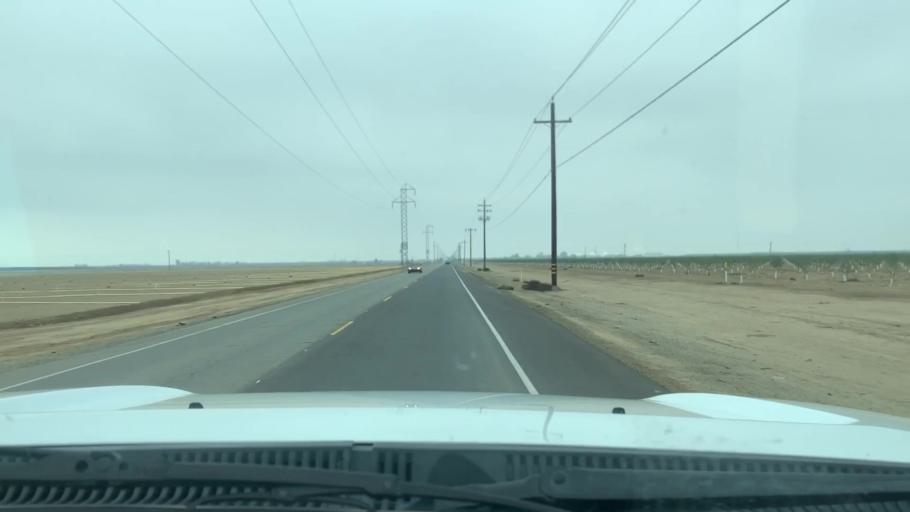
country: US
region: California
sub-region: Kern County
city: Shafter
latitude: 35.4417
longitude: -119.2208
